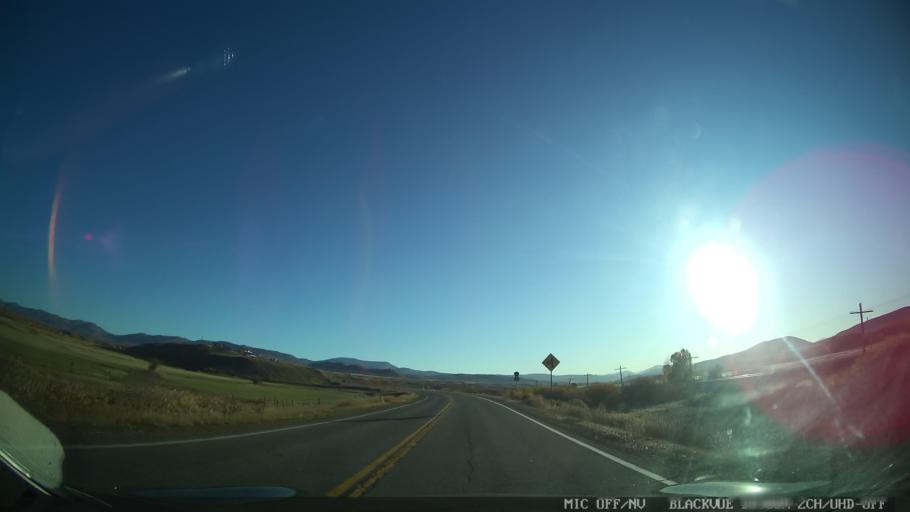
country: US
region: Colorado
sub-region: Grand County
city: Kremmling
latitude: 40.0592
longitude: -106.3045
